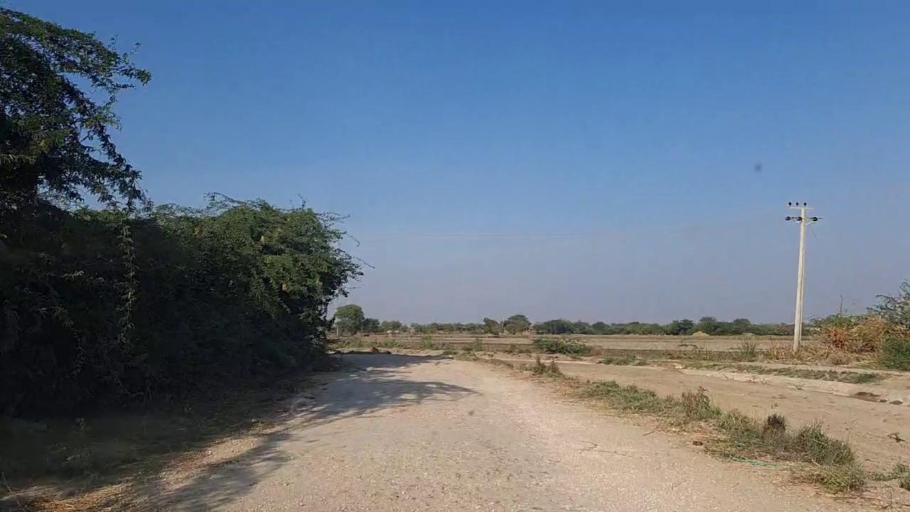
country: PK
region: Sindh
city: Thatta
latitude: 24.7427
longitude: 67.9683
